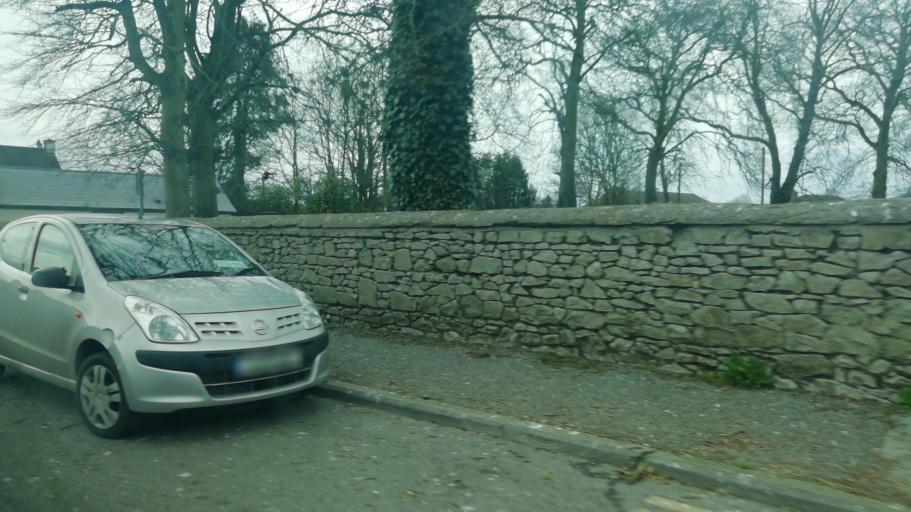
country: IE
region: Leinster
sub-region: Uibh Fhaili
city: Edenderry
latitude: 53.3330
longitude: -7.0685
